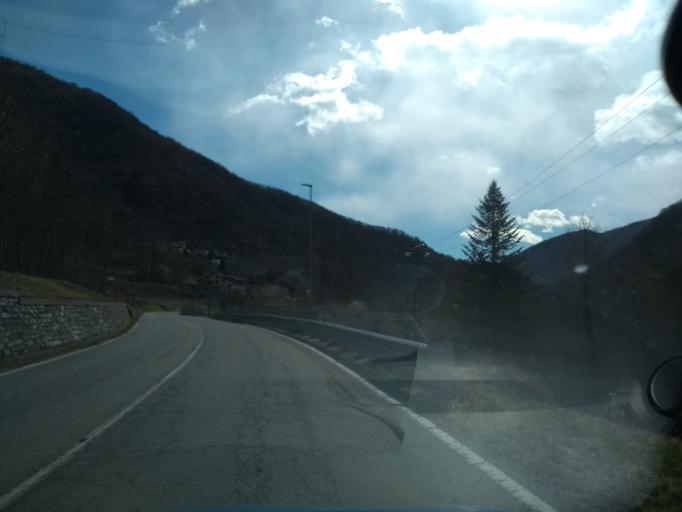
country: IT
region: Piedmont
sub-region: Provincia di Torino
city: Ceres
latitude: 45.3051
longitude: 7.3954
